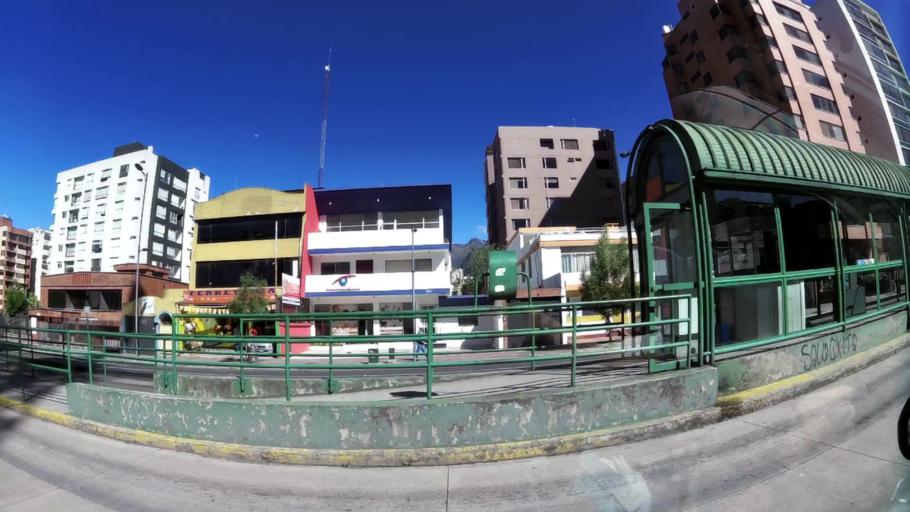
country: EC
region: Pichincha
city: Quito
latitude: -0.1848
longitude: -78.4790
